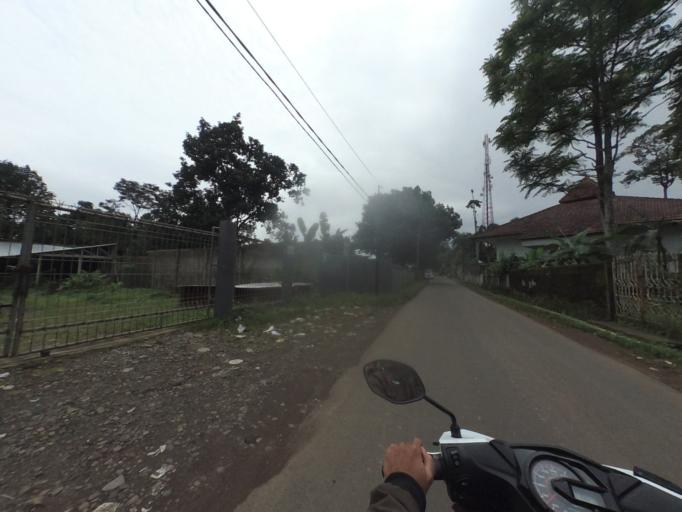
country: ID
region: West Java
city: Bogor
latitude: -6.6369
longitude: 106.7456
